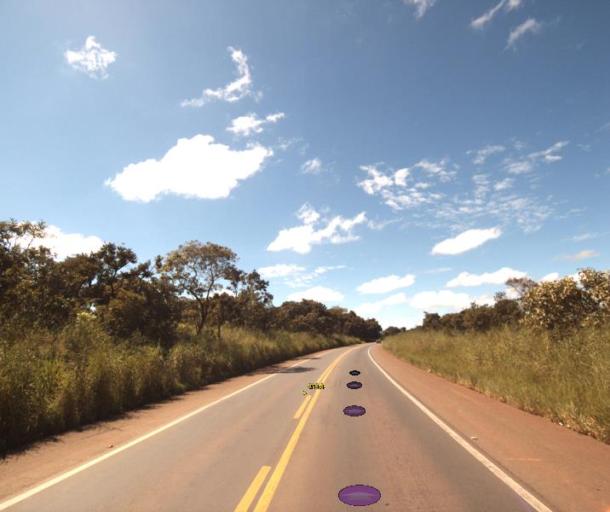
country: BR
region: Goias
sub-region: Rialma
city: Rialma
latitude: -15.3989
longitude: -49.5381
